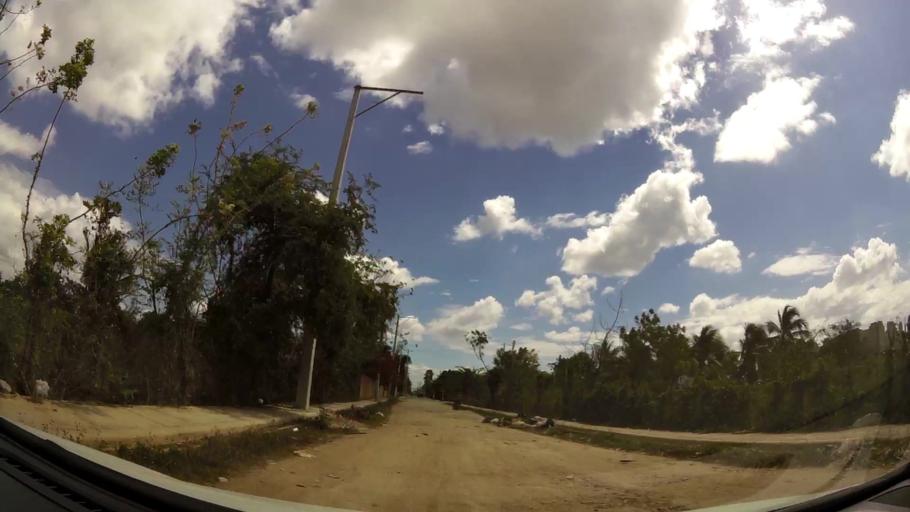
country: DO
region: Santo Domingo
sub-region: Santo Domingo
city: Boca Chica
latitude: 18.4531
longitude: -69.6530
